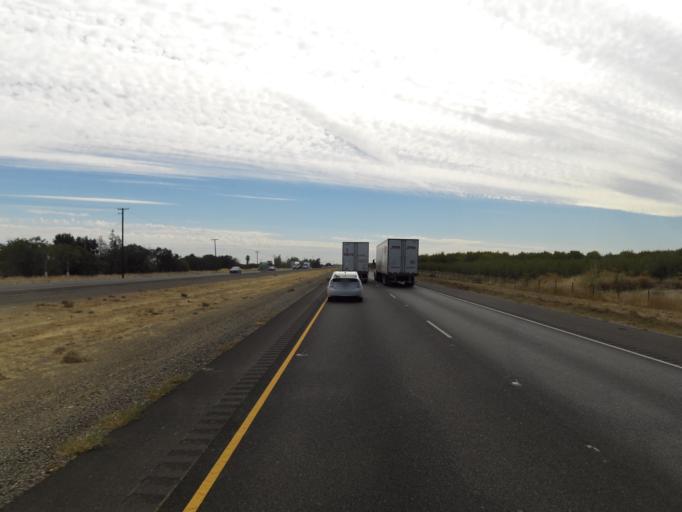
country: US
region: California
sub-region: Colusa County
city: Arbuckle
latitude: 38.9989
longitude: -122.0453
